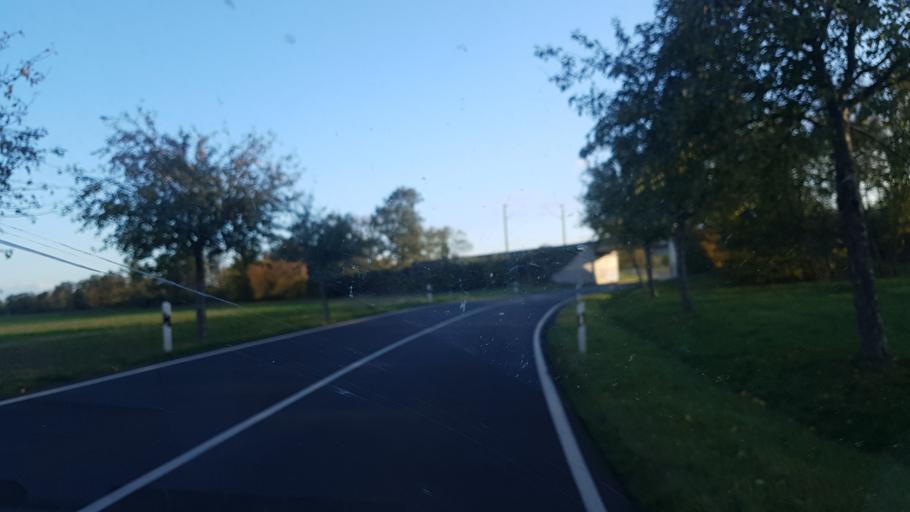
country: DE
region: Saxony
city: Oschatz
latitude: 51.3280
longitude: 13.0544
